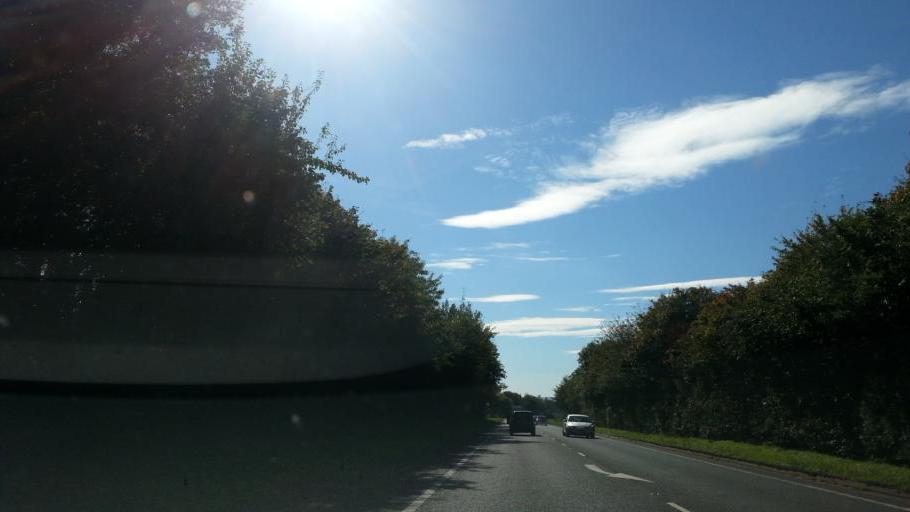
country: GB
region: England
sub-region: Telford and Wrekin
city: Chetwynd
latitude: 52.7396
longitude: -2.4070
